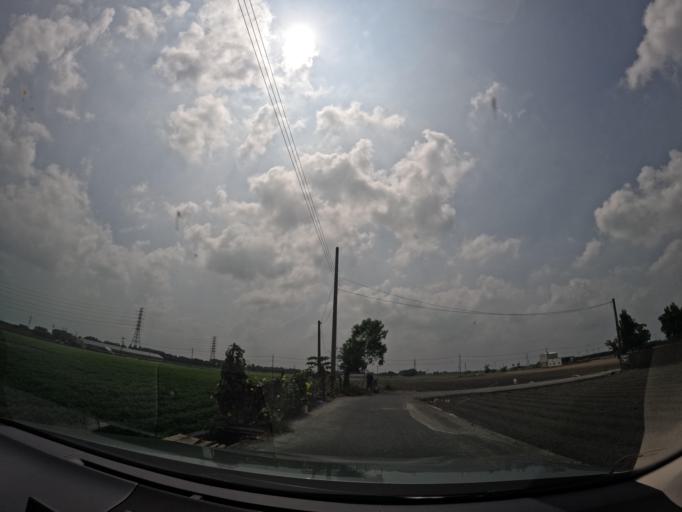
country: TW
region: Taiwan
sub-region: Yunlin
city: Douliu
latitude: 23.6439
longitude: 120.3782
